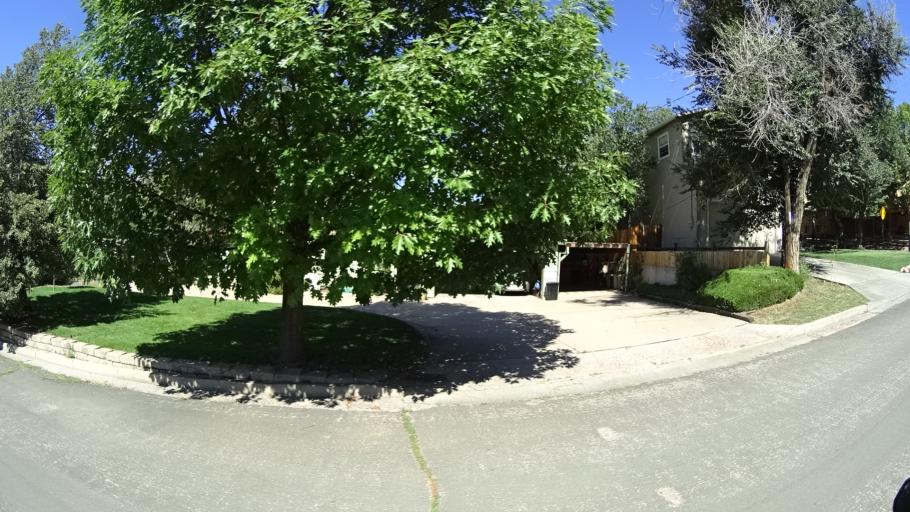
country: US
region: Colorado
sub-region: El Paso County
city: Manitou Springs
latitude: 38.8585
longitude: -104.8745
